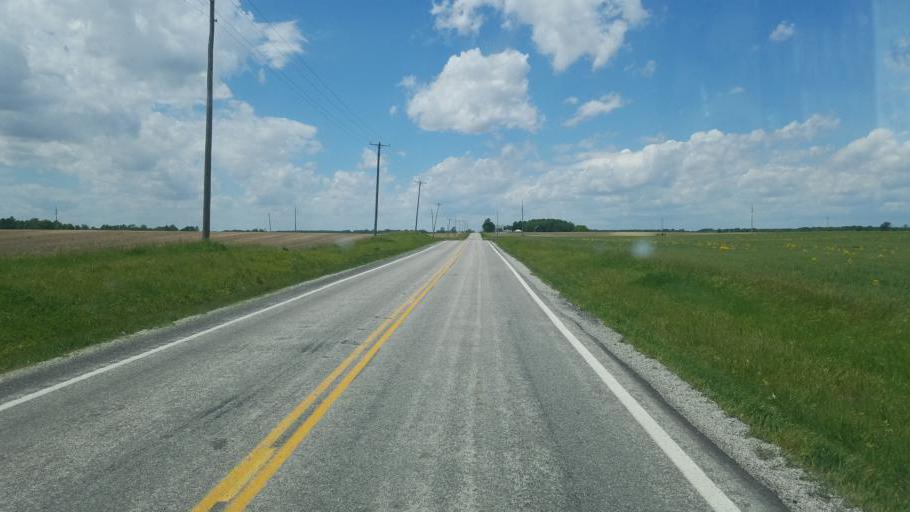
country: US
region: Ohio
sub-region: Huron County
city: Willard
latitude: 41.1051
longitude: -82.6981
